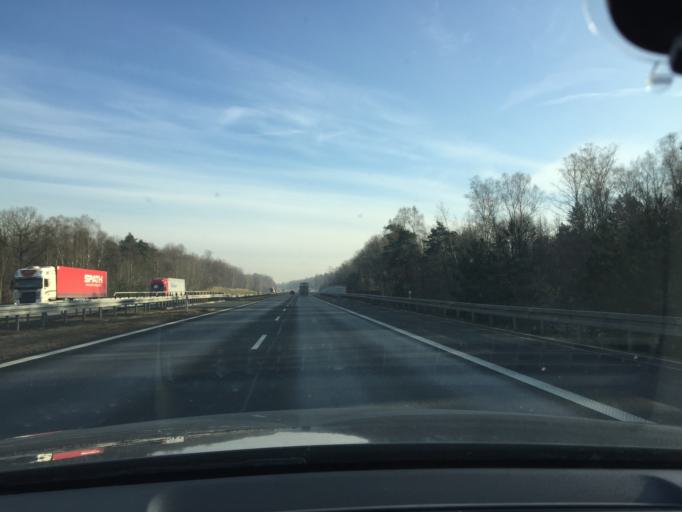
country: PL
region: Silesian Voivodeship
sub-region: Katowice
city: Murcki
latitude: 50.2253
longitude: 19.0847
